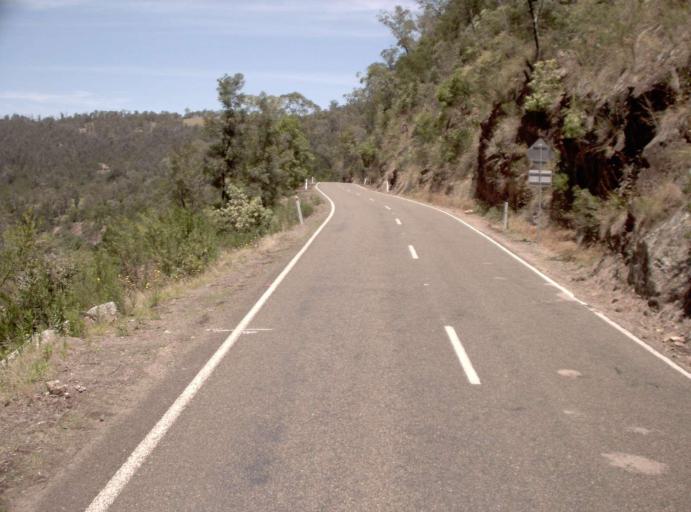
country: AU
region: Victoria
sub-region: East Gippsland
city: Bairnsdale
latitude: -37.4762
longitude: 147.8318
